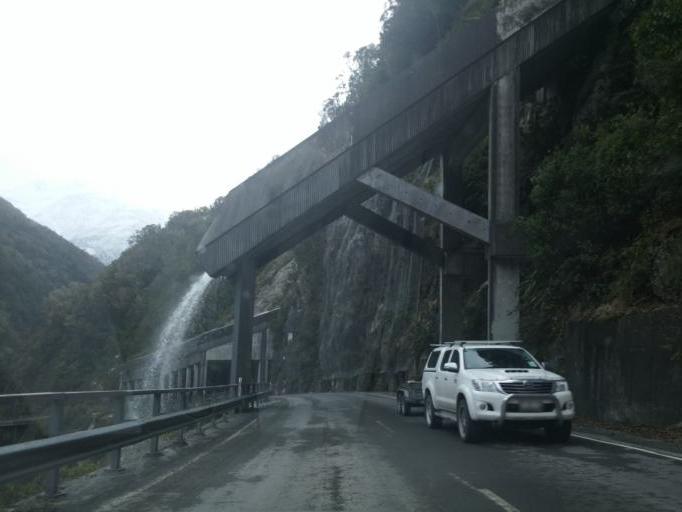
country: NZ
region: West Coast
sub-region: Grey District
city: Greymouth
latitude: -42.8791
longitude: 171.5571
